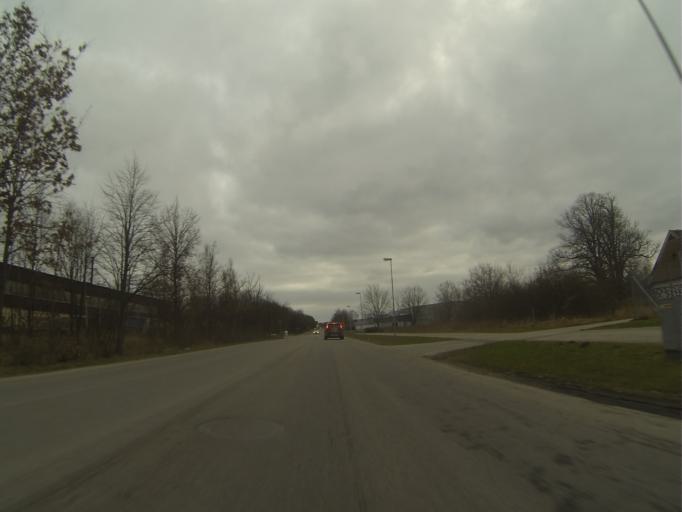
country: SE
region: Skane
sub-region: Svedala Kommun
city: Svedala
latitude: 55.5121
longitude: 13.2521
